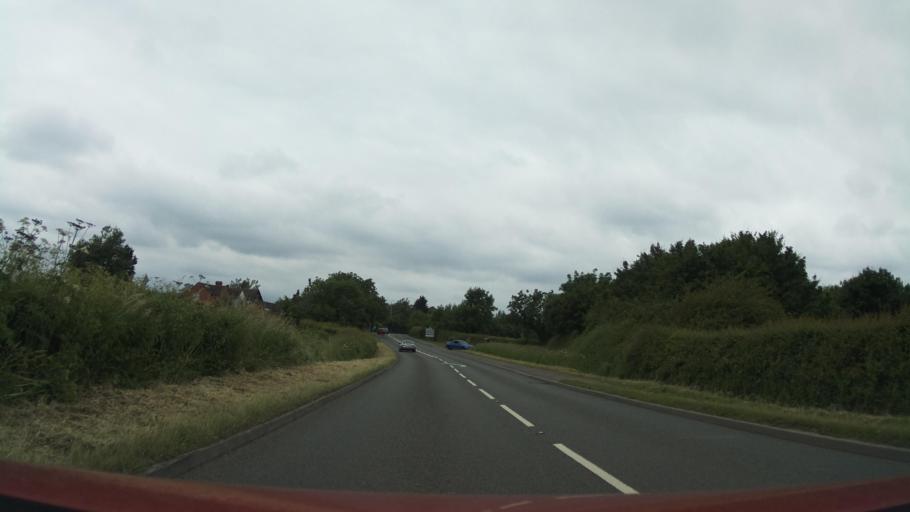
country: GB
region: England
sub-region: Leicestershire
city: Melton Mowbray
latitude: 52.7480
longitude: -0.8692
